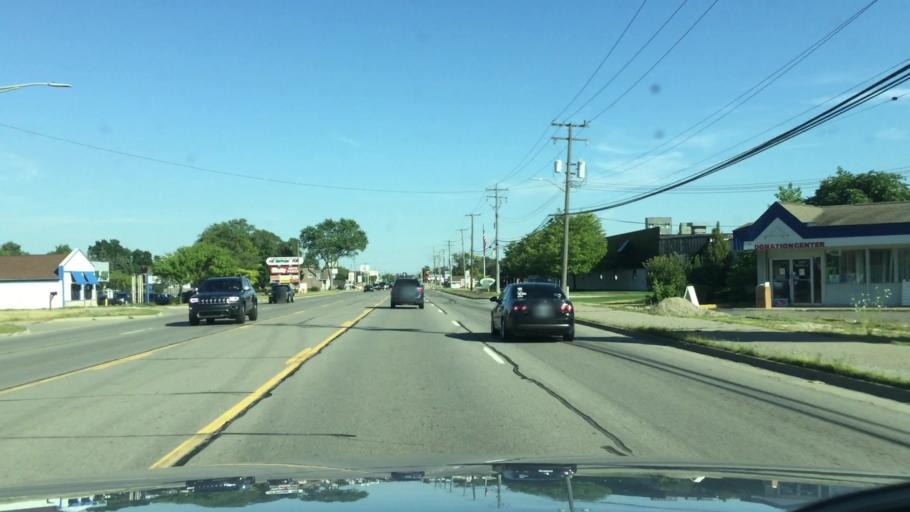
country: US
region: Michigan
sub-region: Oakland County
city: Waterford
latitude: 42.6971
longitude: -83.3957
